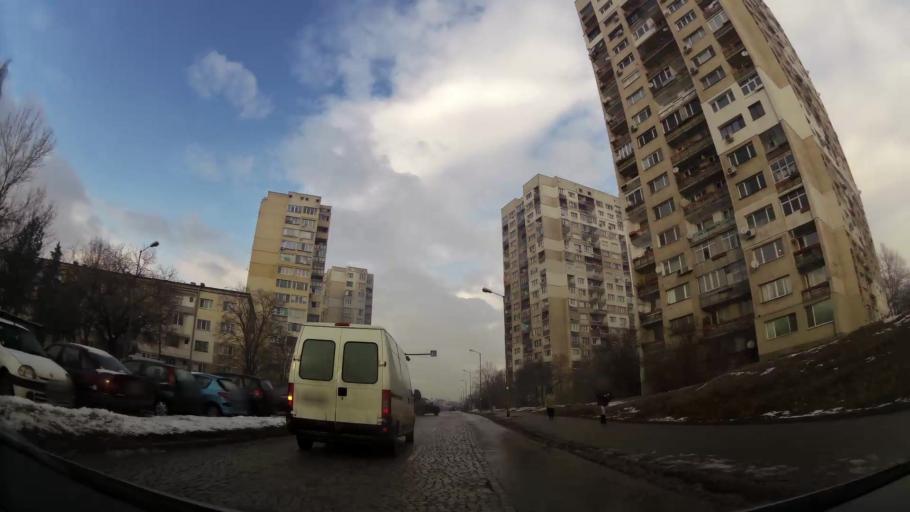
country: BG
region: Sofia-Capital
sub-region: Stolichna Obshtina
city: Sofia
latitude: 42.6968
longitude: 23.2792
